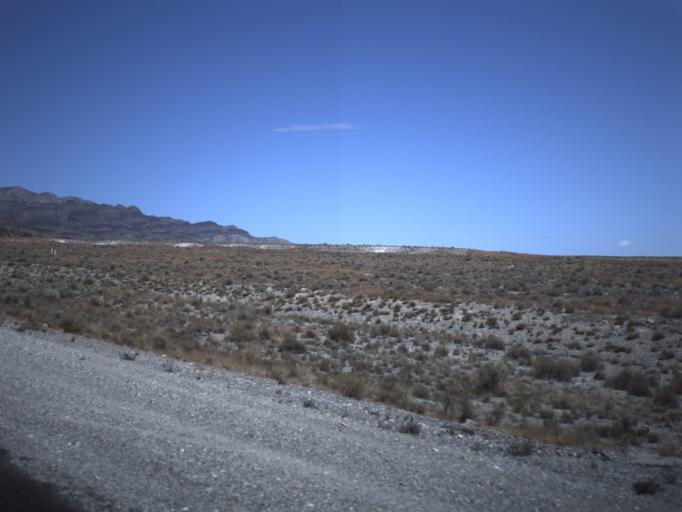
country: US
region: Utah
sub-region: Beaver County
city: Milford
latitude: 39.0832
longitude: -113.4959
